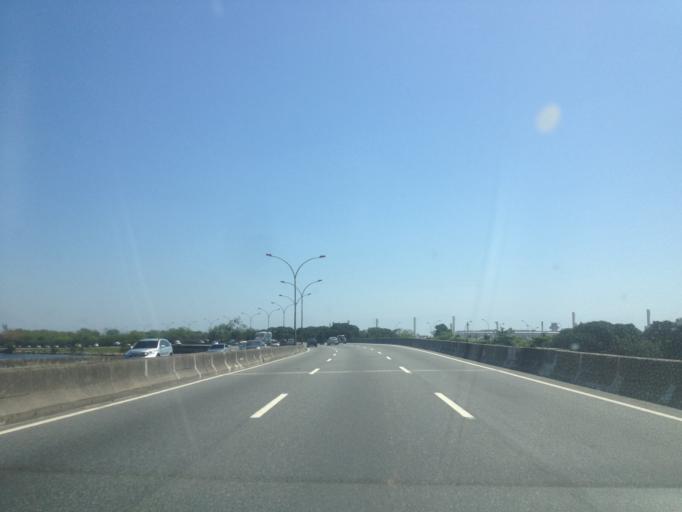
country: BR
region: Rio de Janeiro
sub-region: Duque De Caxias
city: Duque de Caxias
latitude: -22.8249
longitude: -43.2514
